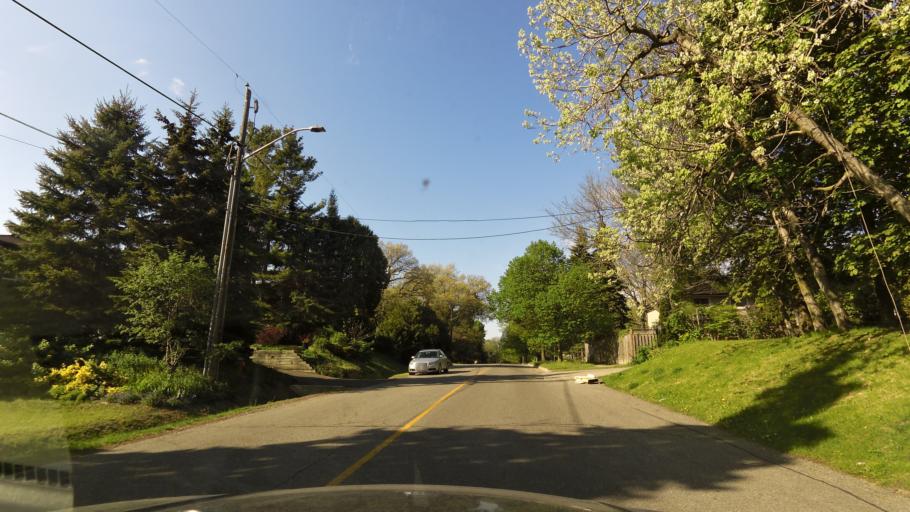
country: CA
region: Ontario
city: Mississauga
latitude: 43.5590
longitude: -79.6068
